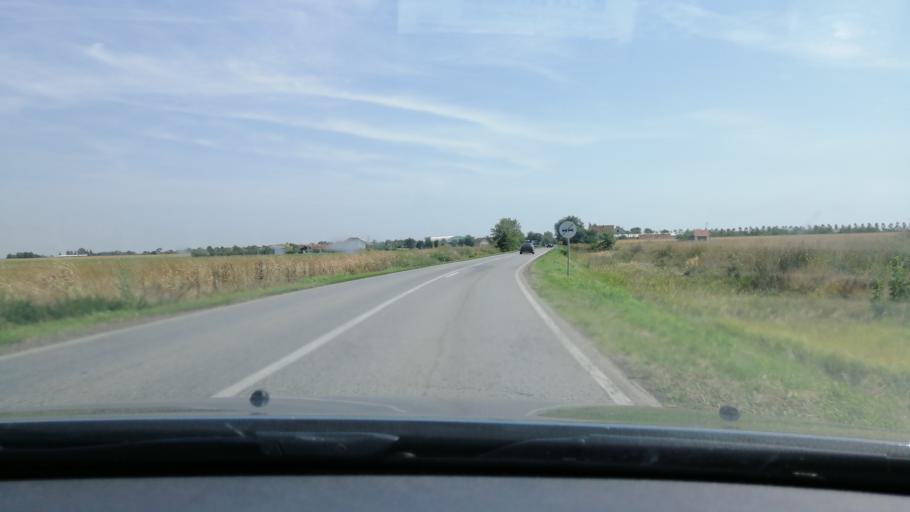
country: RS
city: Lazarevo
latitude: 45.3889
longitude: 20.5198
